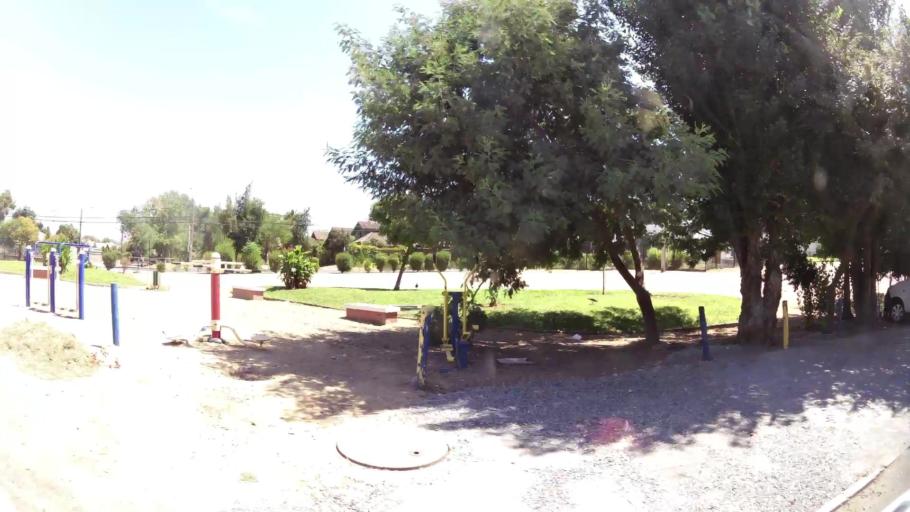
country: CL
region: Maule
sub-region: Provincia de Talca
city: Talca
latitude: -35.4271
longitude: -71.6311
